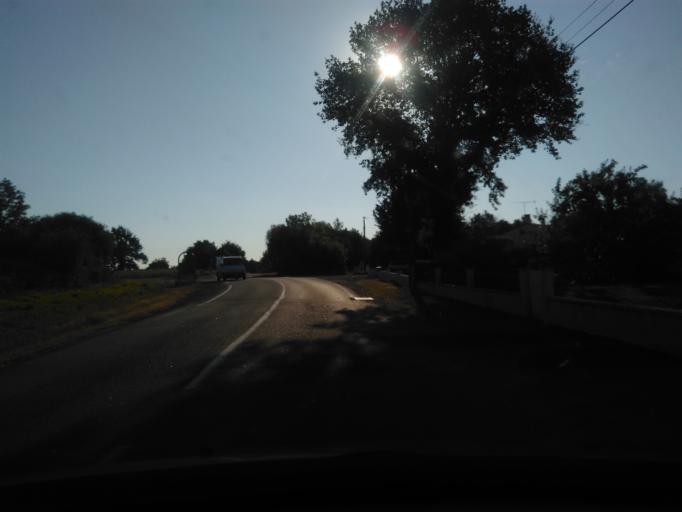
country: FR
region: Pays de la Loire
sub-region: Departement de la Vendee
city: Dompierre-sur-Yon
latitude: 46.7393
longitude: -1.4075
